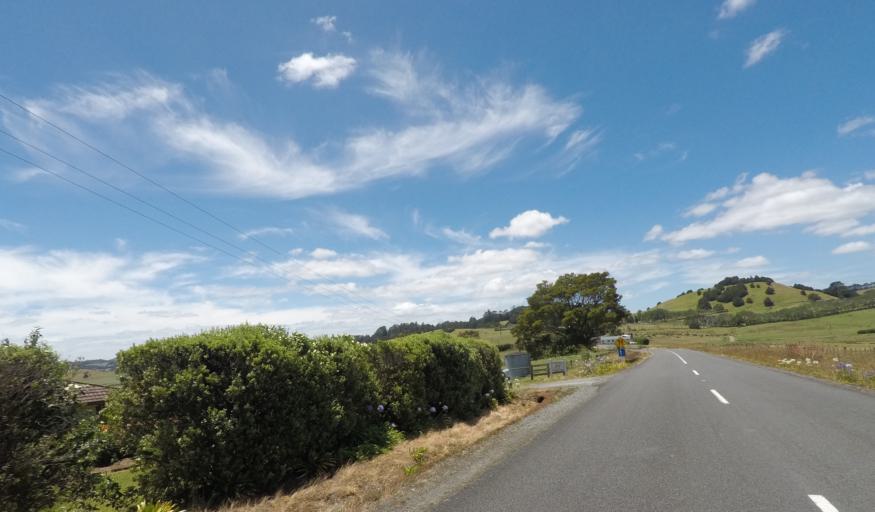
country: NZ
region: Northland
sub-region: Whangarei
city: Whangarei
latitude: -35.5600
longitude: 174.2845
